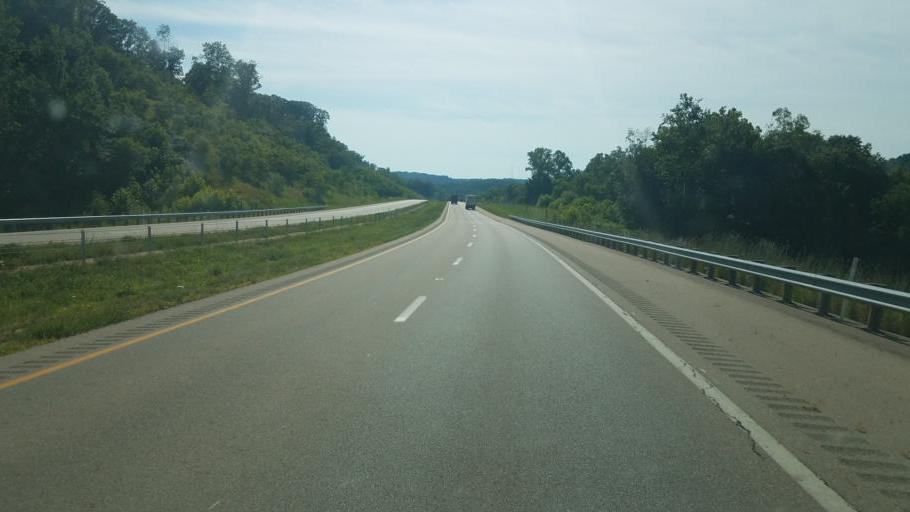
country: US
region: Ohio
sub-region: Athens County
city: Nelsonville
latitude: 39.4777
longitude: -82.2986
